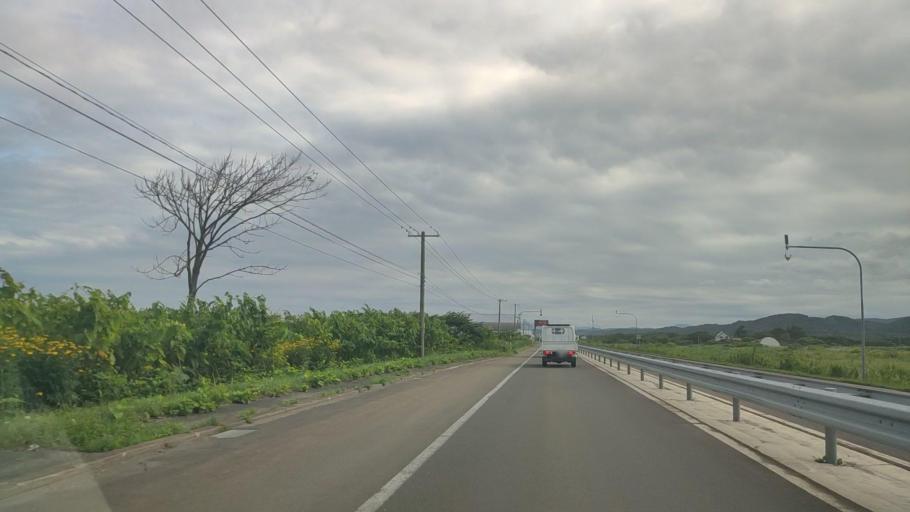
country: JP
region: Hokkaido
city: Niseko Town
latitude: 42.4482
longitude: 140.3302
